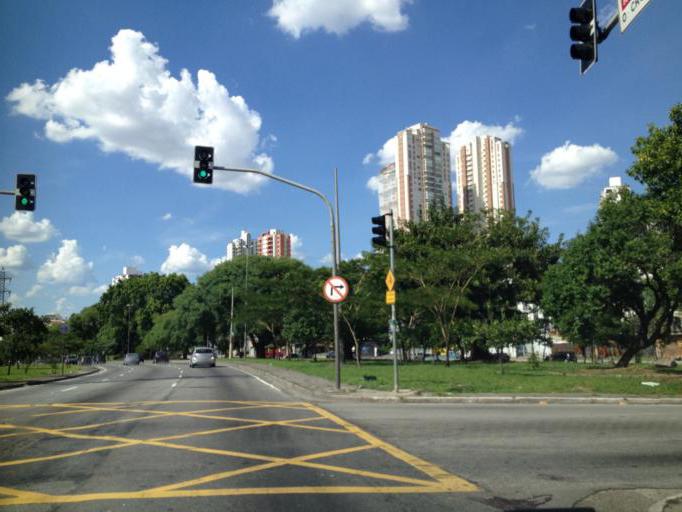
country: BR
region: Sao Paulo
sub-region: Sao Paulo
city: Sao Paulo
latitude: -23.5547
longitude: -46.5768
